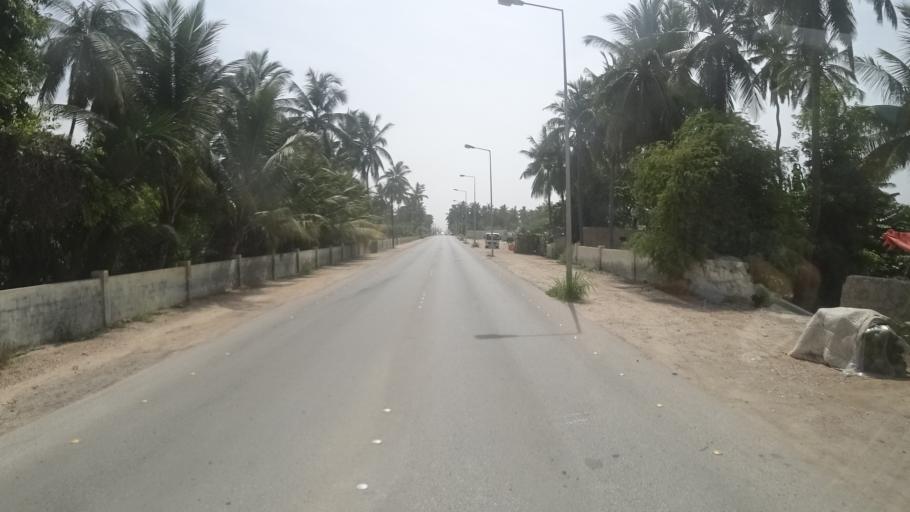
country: OM
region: Zufar
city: Salalah
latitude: 17.0160
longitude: 54.1536
